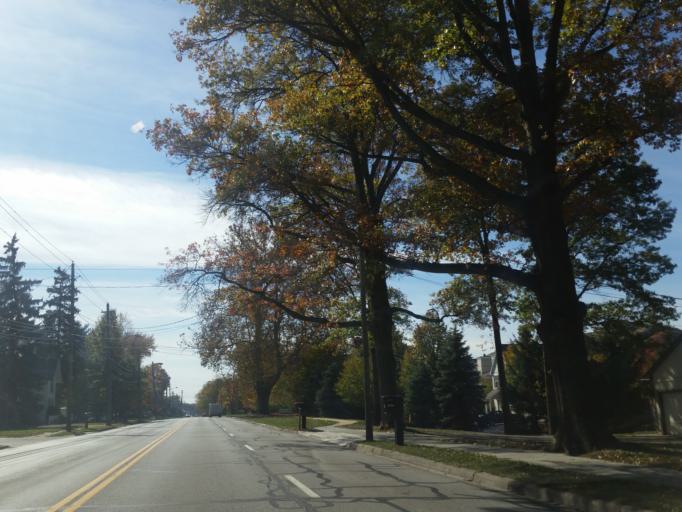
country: US
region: Ohio
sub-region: Cuyahoga County
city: Westlake
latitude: 41.4420
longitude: -81.9350
